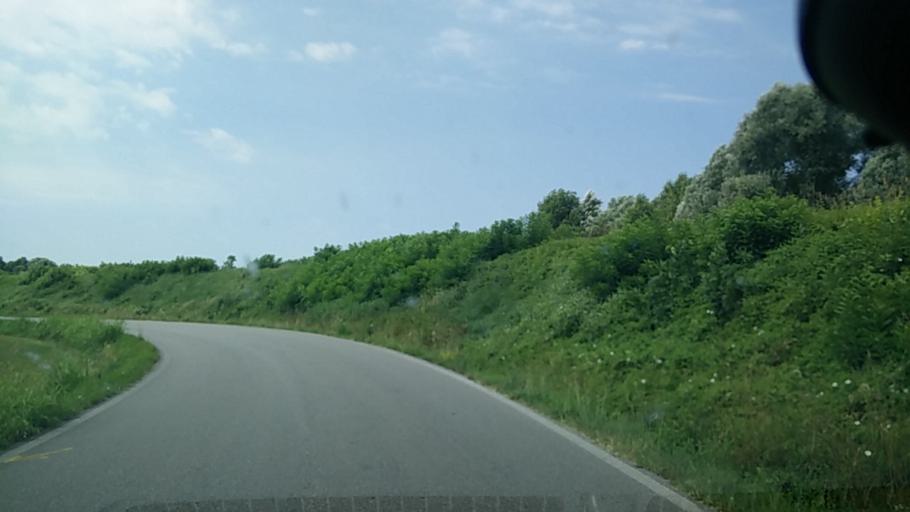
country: IT
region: Friuli Venezia Giulia
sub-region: Provincia di Pordenone
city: Puia-Villanova
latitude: 45.8339
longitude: 12.5734
